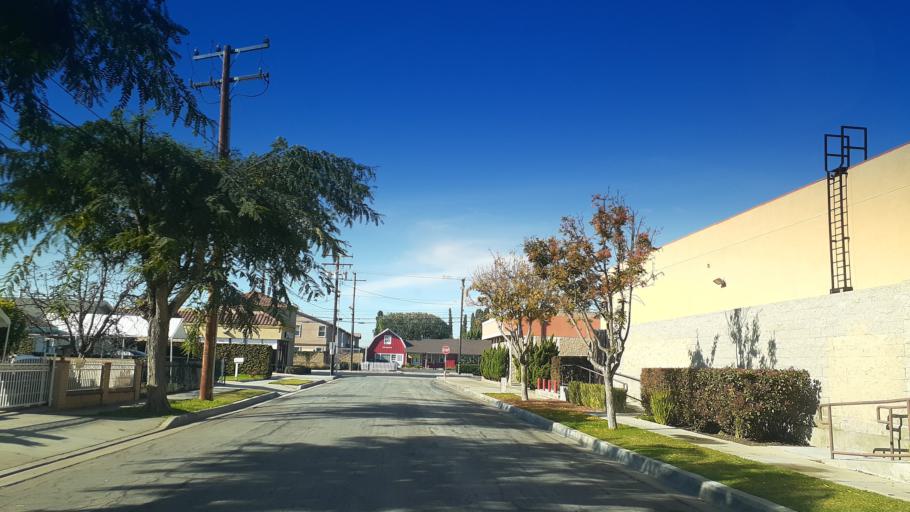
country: US
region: California
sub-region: Los Angeles County
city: Cerritos
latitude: 33.8578
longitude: -118.0713
